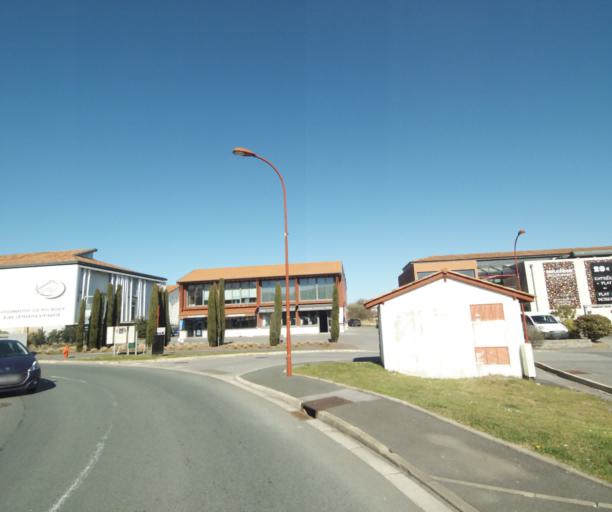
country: FR
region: Aquitaine
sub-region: Departement des Pyrenees-Atlantiques
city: Ciboure
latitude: 43.3836
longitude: -1.6927
